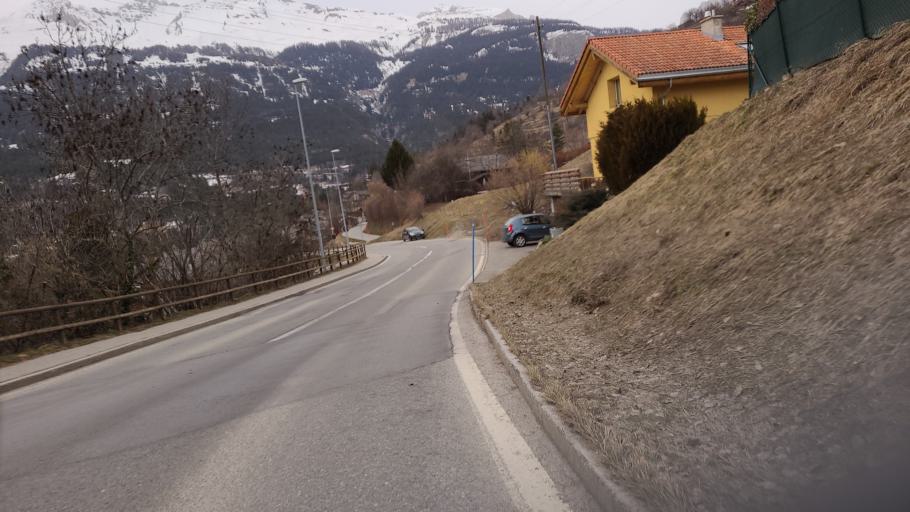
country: CH
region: Valais
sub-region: Sierre District
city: Lens
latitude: 46.2889
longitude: 7.4413
